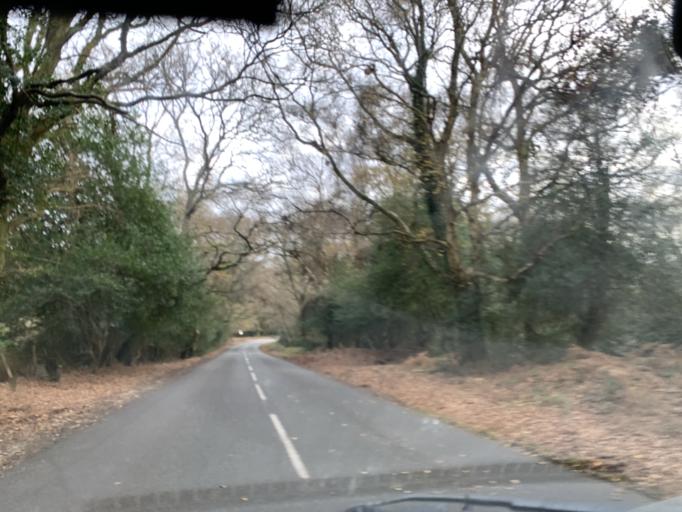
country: GB
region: England
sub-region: Hampshire
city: Lyndhurst
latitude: 50.8909
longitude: -1.6157
